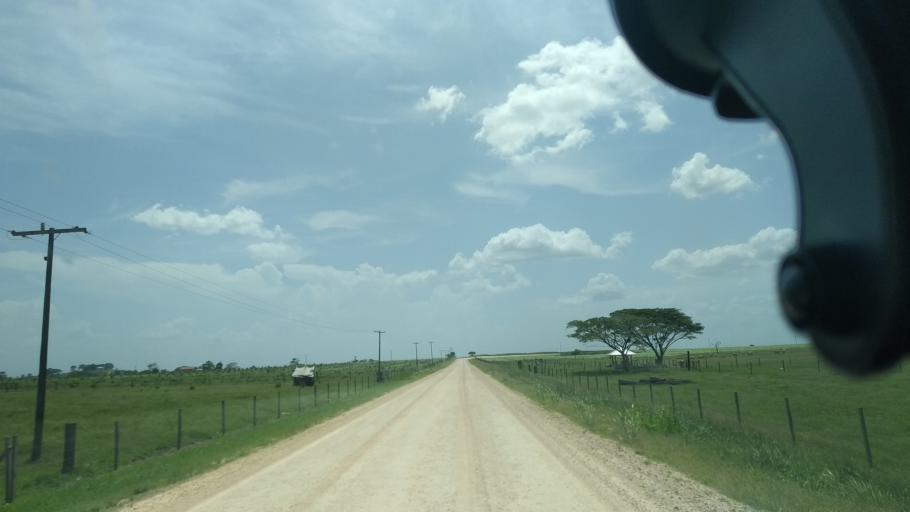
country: BZ
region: Cayo
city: San Ignacio
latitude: 17.3148
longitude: -89.0419
